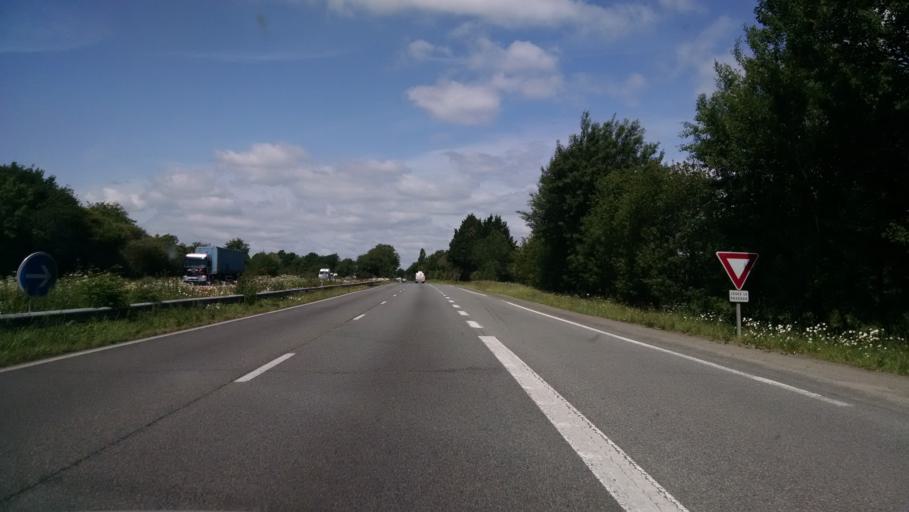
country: FR
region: Pays de la Loire
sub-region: Departement de la Loire-Atlantique
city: Le Temple-de-Bretagne
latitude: 47.3361
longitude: -1.8009
